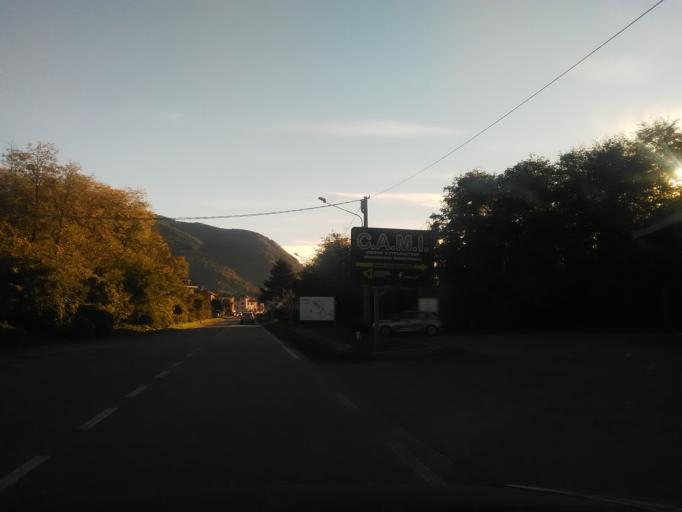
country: IT
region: Piedmont
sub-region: Provincia di Vercelli
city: Borgosesia
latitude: 45.6969
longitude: 8.2822
